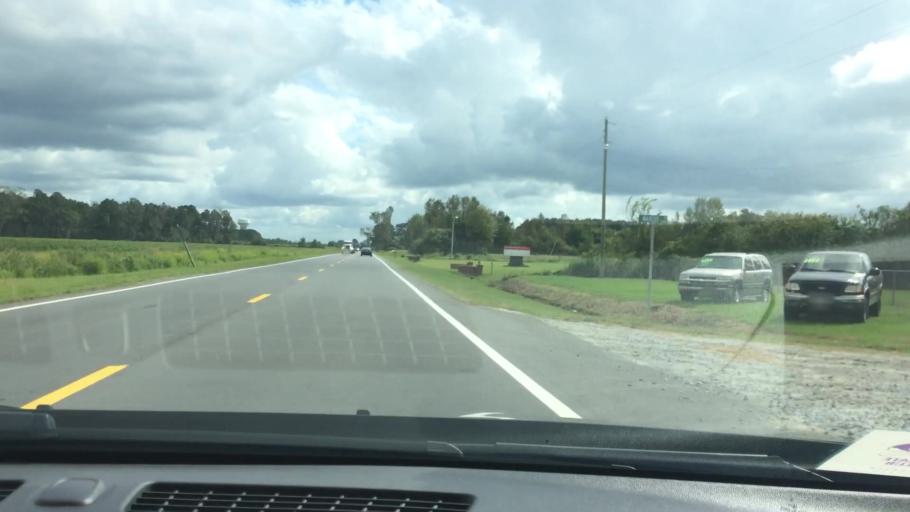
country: US
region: North Carolina
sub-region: Pitt County
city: Farmville
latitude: 35.5588
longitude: -77.5587
